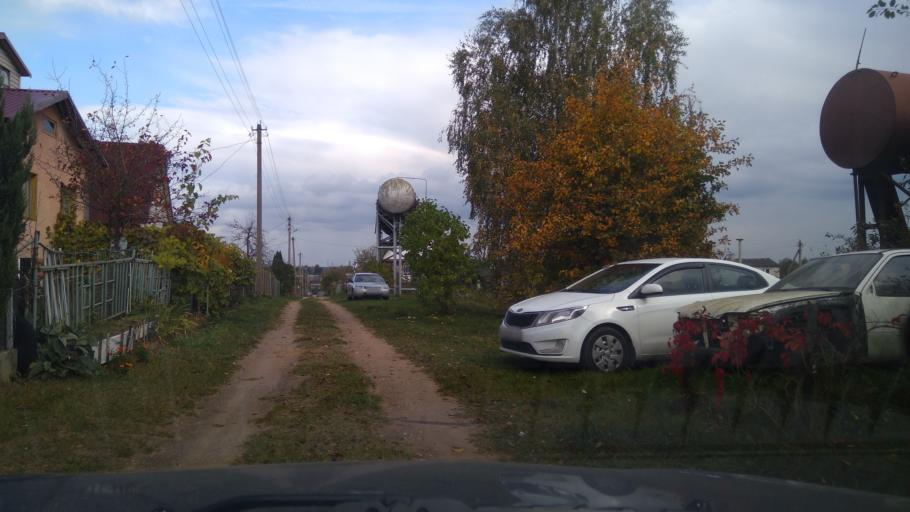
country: BY
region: Minsk
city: Rudzyensk
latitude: 53.6052
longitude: 27.8439
